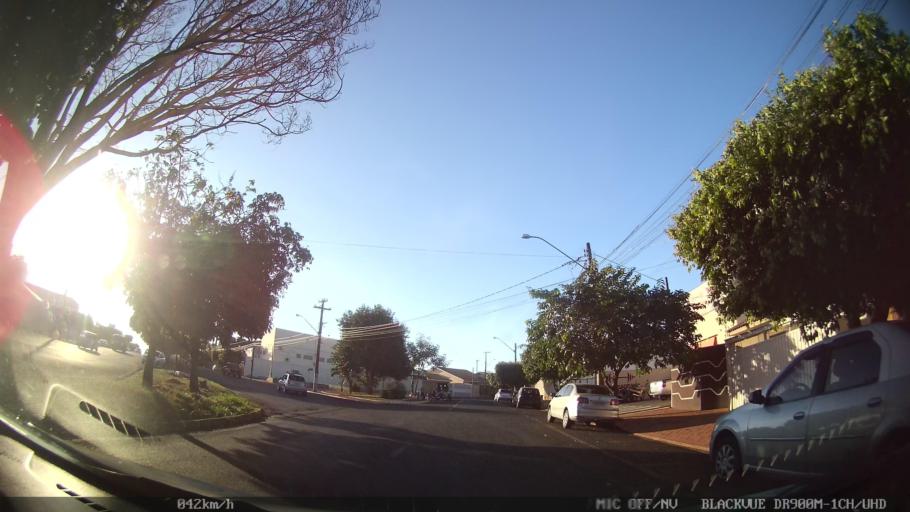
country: BR
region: Sao Paulo
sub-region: Sao Jose Do Rio Preto
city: Sao Jose do Rio Preto
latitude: -20.7934
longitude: -49.3580
